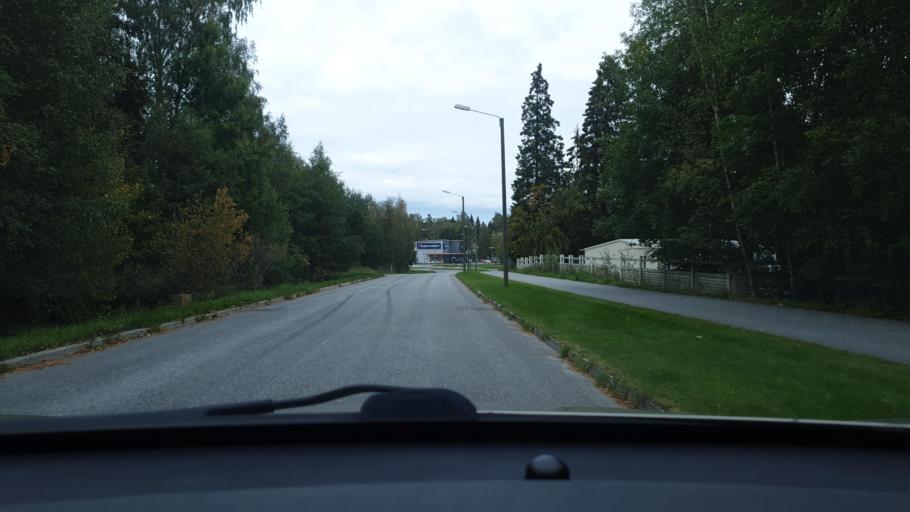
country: FI
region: Ostrobothnia
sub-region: Vaasa
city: Teeriniemi
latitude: 63.0883
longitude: 21.6816
